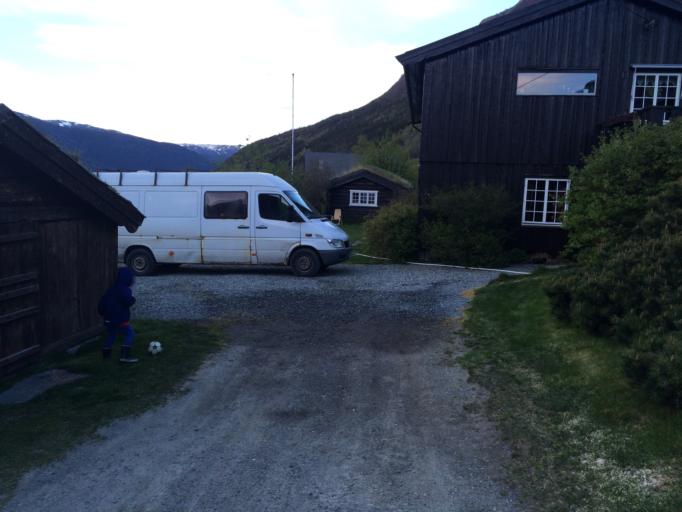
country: NO
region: Oppland
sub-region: Lom
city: Fossbergom
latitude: 61.8184
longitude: 8.5269
